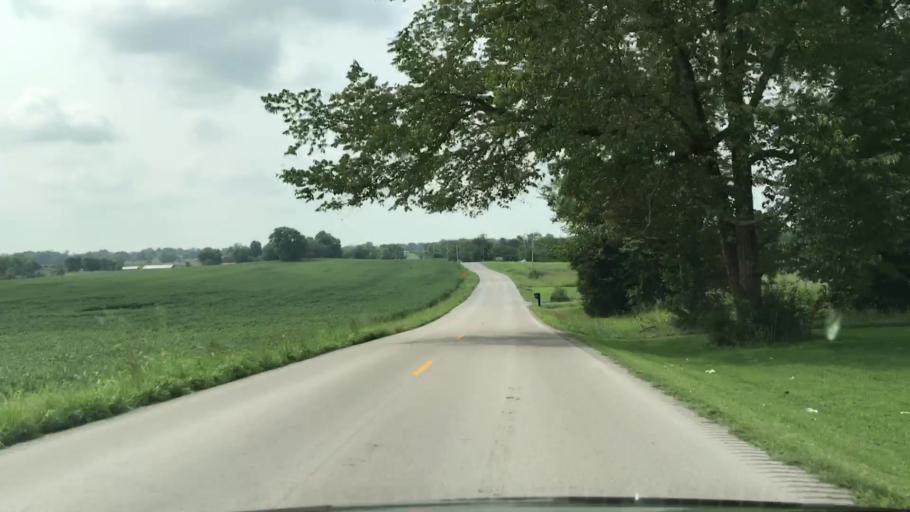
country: US
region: Kentucky
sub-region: Edmonson County
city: Brownsville
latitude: 37.0980
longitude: -86.1473
